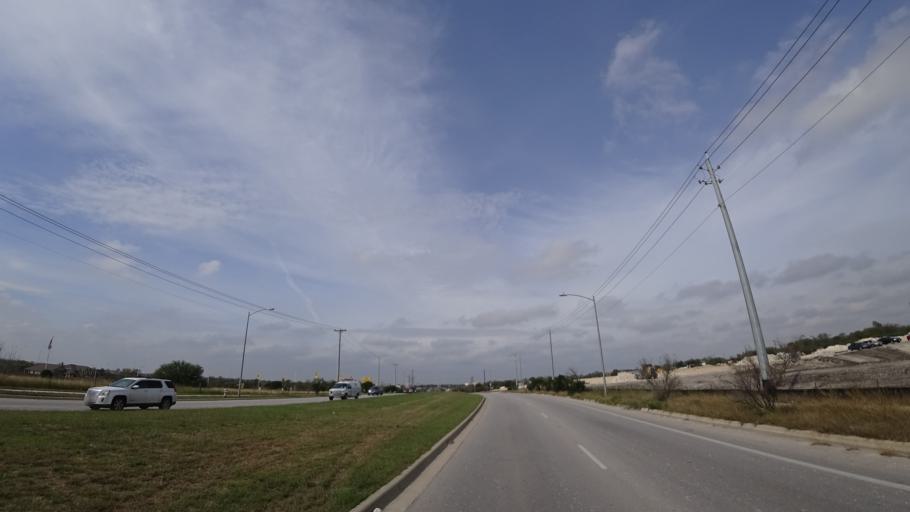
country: US
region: Texas
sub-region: Travis County
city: Windemere
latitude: 30.4354
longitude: -97.6545
